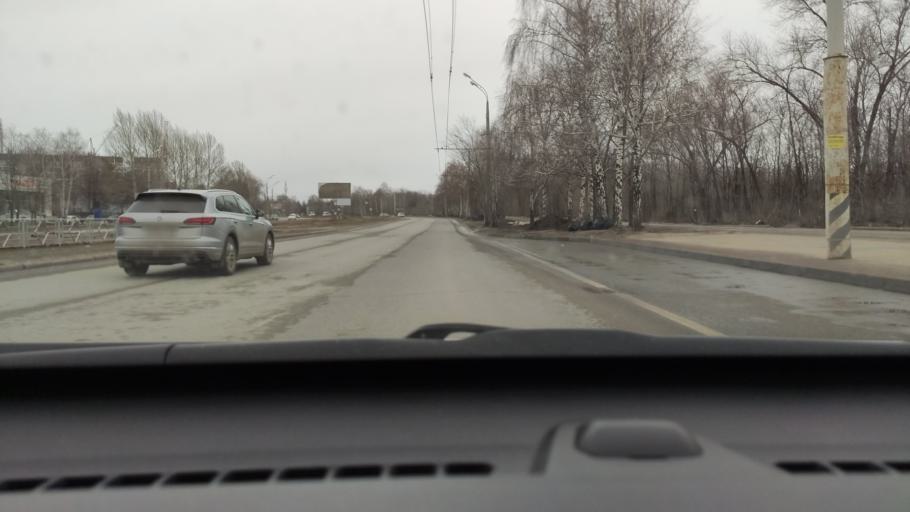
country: RU
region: Samara
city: Tol'yatti
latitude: 53.5025
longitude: 49.2640
